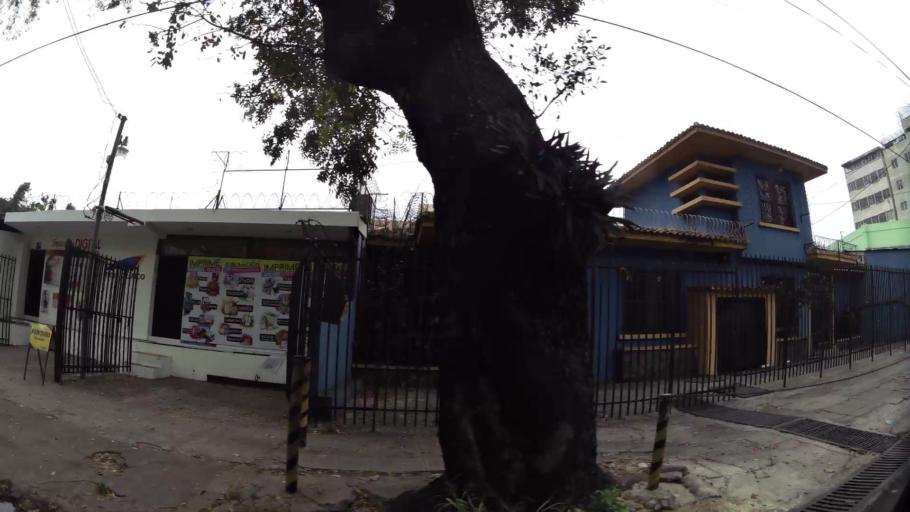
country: SV
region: San Salvador
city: San Salvador
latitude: 13.7011
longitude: -89.2028
